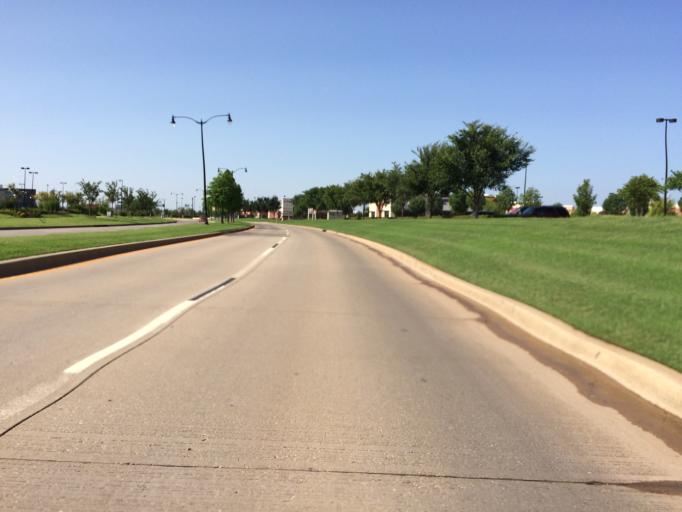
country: US
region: Oklahoma
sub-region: Cleveland County
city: Norman
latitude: 35.2404
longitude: -97.4823
